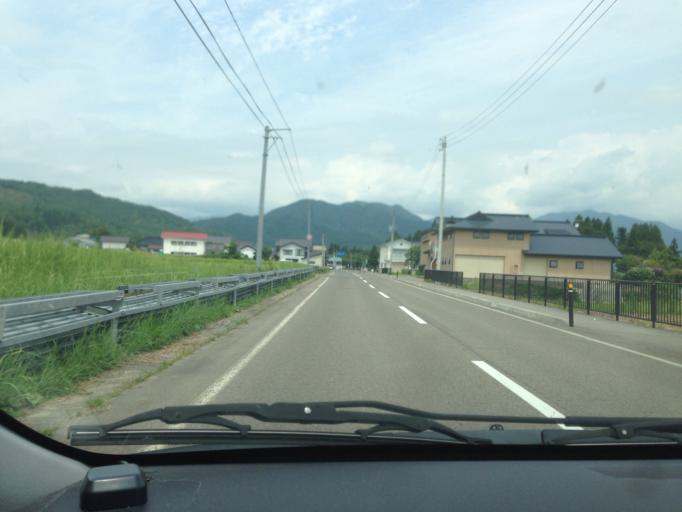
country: JP
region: Fukushima
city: Kitakata
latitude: 37.7065
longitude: 139.8466
